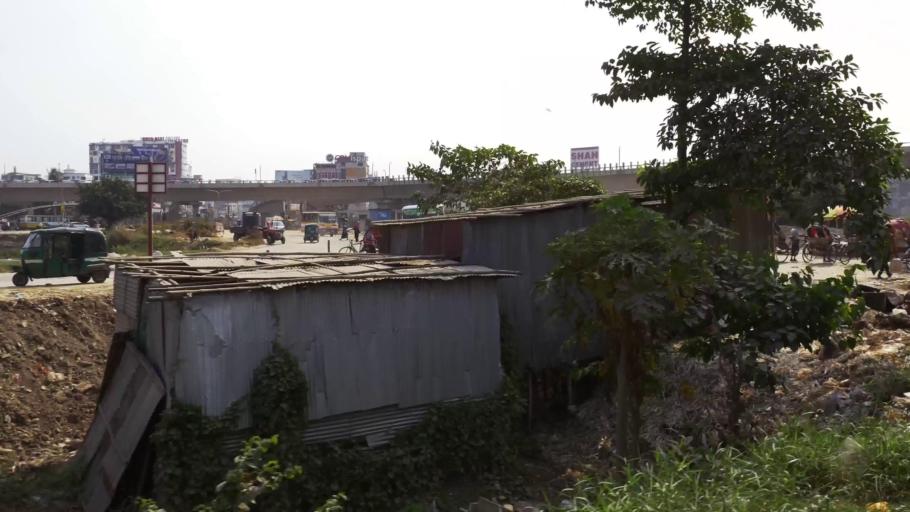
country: BD
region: Dhaka
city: Tungi
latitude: 23.8778
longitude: 90.4060
